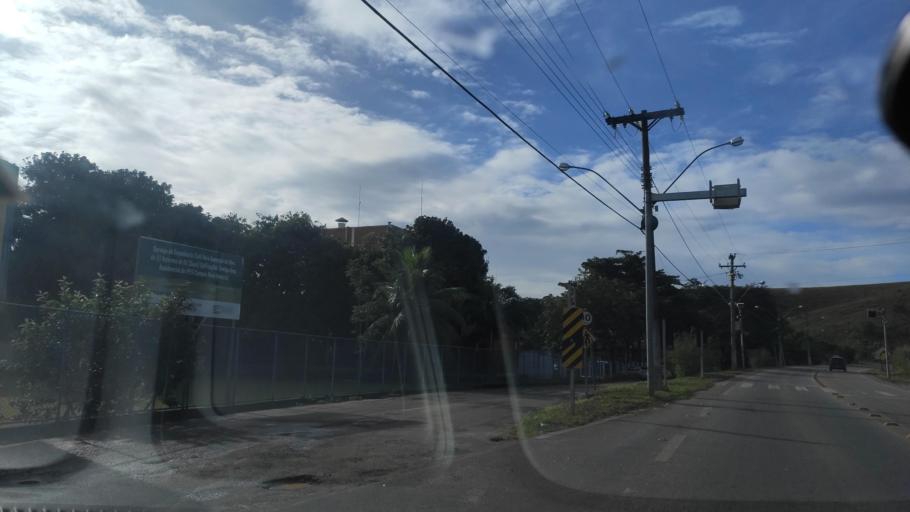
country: BR
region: Espirito Santo
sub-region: Nova Venecia
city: Nova Venecia
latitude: -18.7135
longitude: -40.3788
